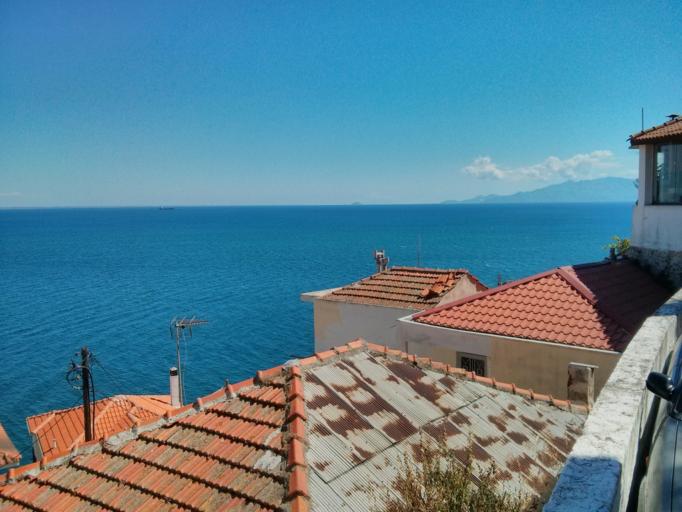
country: GR
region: East Macedonia and Thrace
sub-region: Nomos Kavalas
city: Kavala
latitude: 40.9348
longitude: 24.4175
